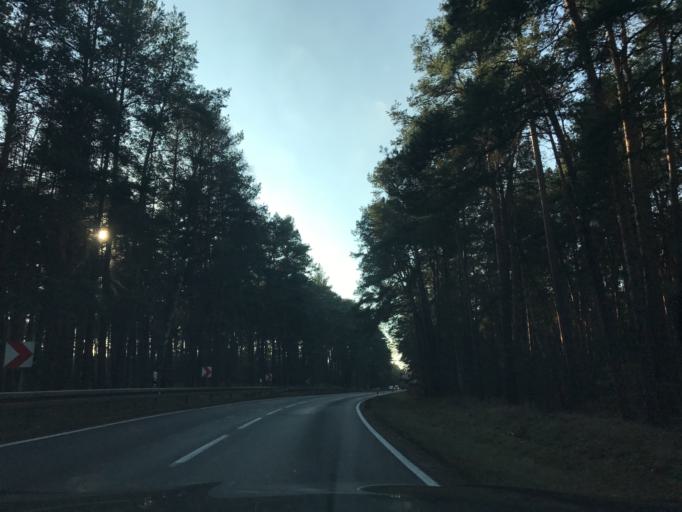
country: DE
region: Brandenburg
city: Wenzlow
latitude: 52.3087
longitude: 12.4747
